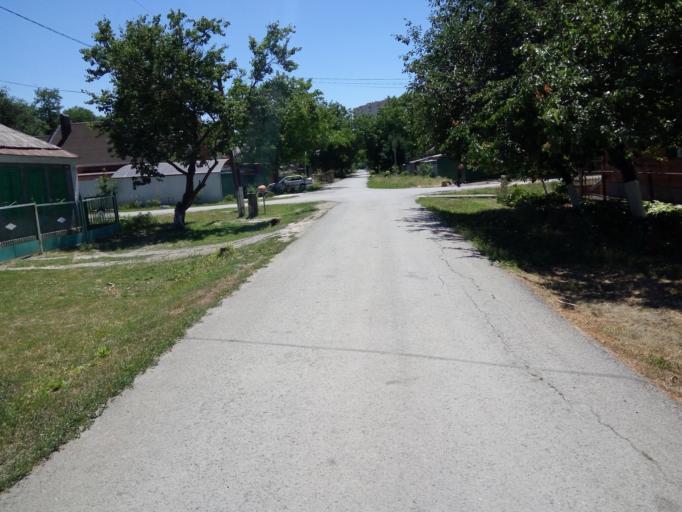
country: RU
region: Rostov
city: Bataysk
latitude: 47.1420
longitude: 39.7709
